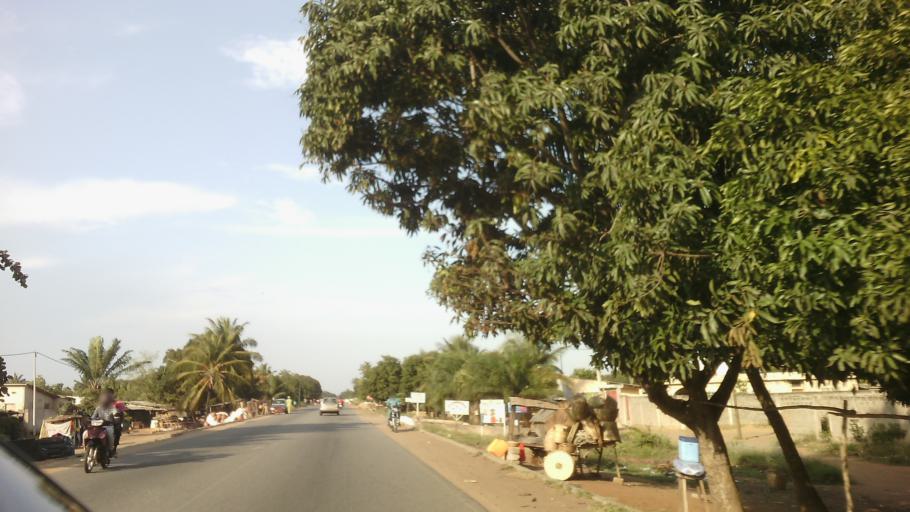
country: TG
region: Maritime
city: Lome
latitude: 6.1935
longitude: 1.3978
